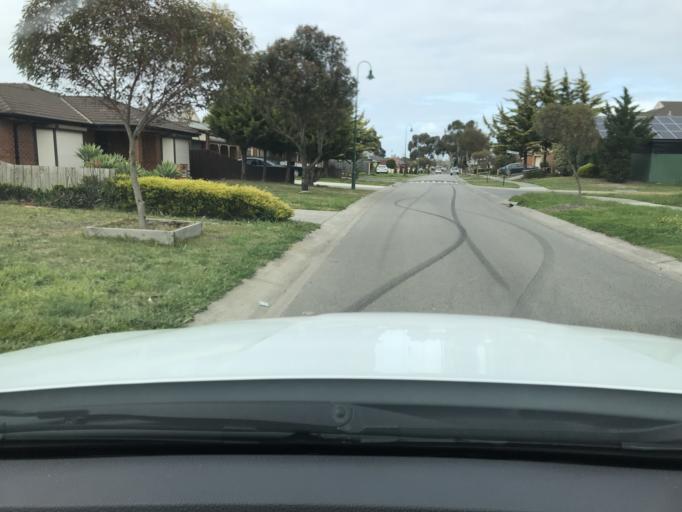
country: AU
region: Victoria
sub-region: Hume
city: Roxburgh Park
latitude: -37.6048
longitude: 144.9240
